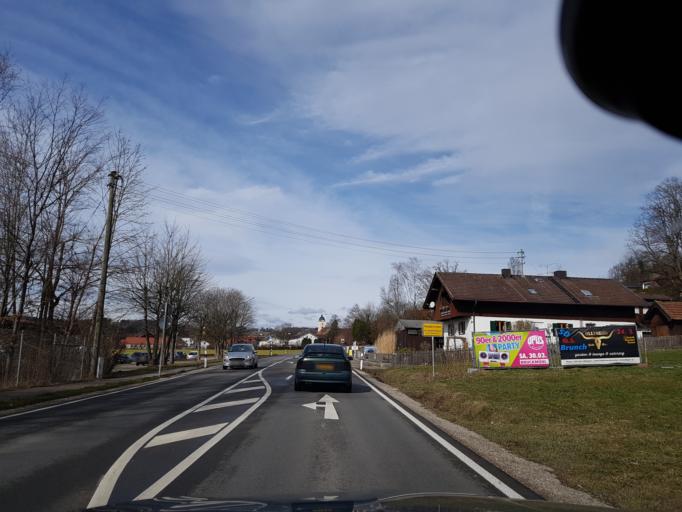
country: DE
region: Bavaria
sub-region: Upper Bavaria
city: Feldkirchen-Westerham
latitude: 47.9066
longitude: 11.8528
